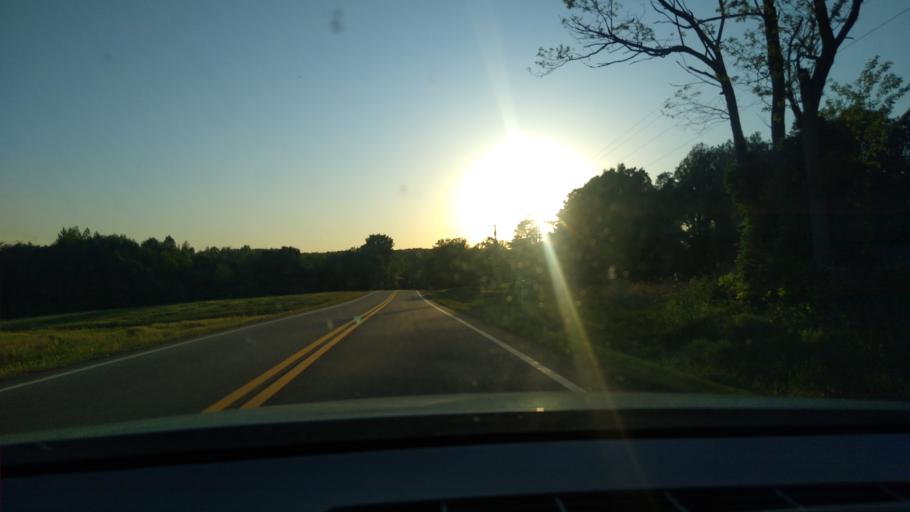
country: US
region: North Carolina
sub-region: Caswell County
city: Yanceyville
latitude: 36.3864
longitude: -79.4907
